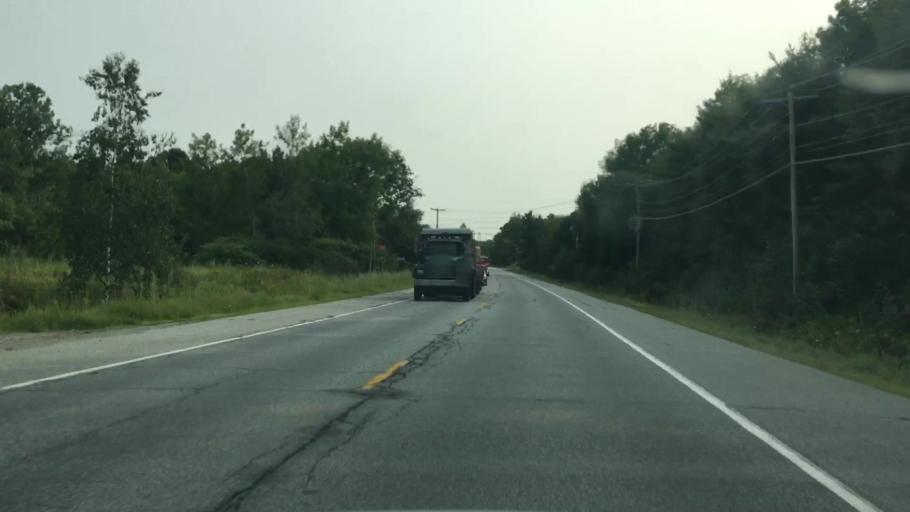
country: US
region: Maine
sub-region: Kennebec County
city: Gardiner
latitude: 44.1968
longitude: -69.8047
